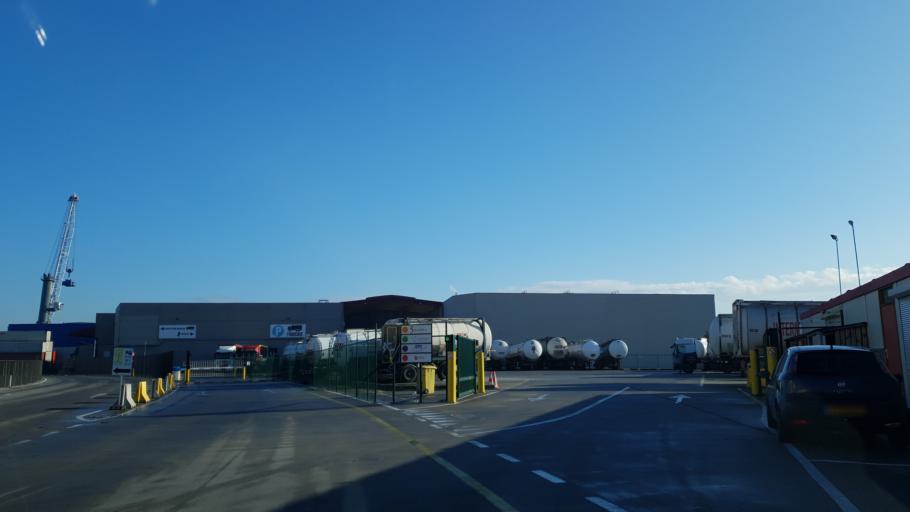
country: BE
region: Flanders
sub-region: Provincie Antwerpen
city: Zwijndrecht
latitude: 51.2452
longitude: 4.3513
